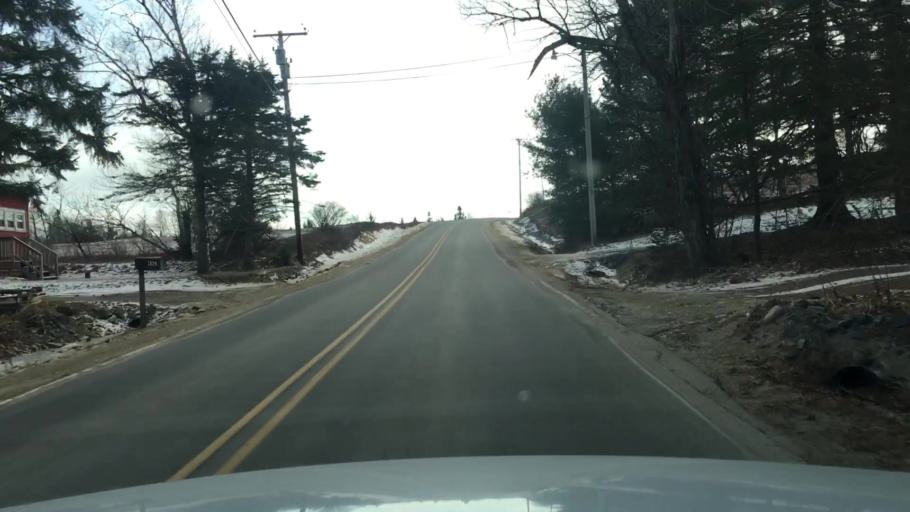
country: US
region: Maine
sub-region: Washington County
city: Jonesport
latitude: 44.6239
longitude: -67.6016
